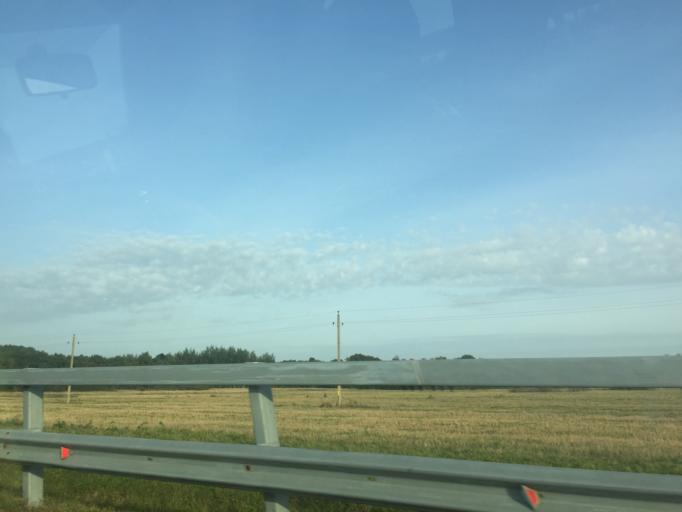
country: RU
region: Kaliningrad
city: Gur'yevsk
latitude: 54.8686
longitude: 20.5679
